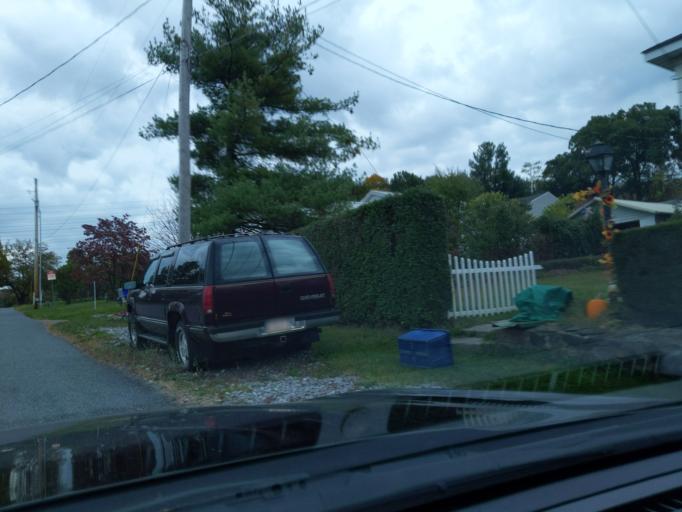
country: US
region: Pennsylvania
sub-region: Blair County
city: Altoona
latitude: 40.4979
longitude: -78.3829
